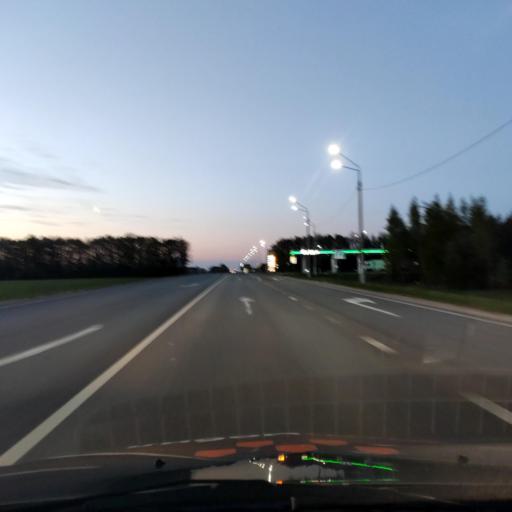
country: RU
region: Orjol
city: Zmiyevka
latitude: 52.7152
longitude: 36.3436
